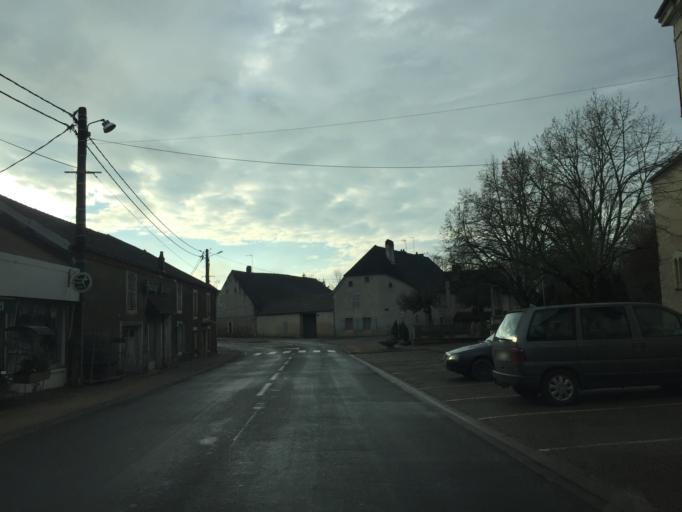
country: FR
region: Franche-Comte
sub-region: Departement du Jura
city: Mont-sous-Vaudrey
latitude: 46.9791
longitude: 5.6024
